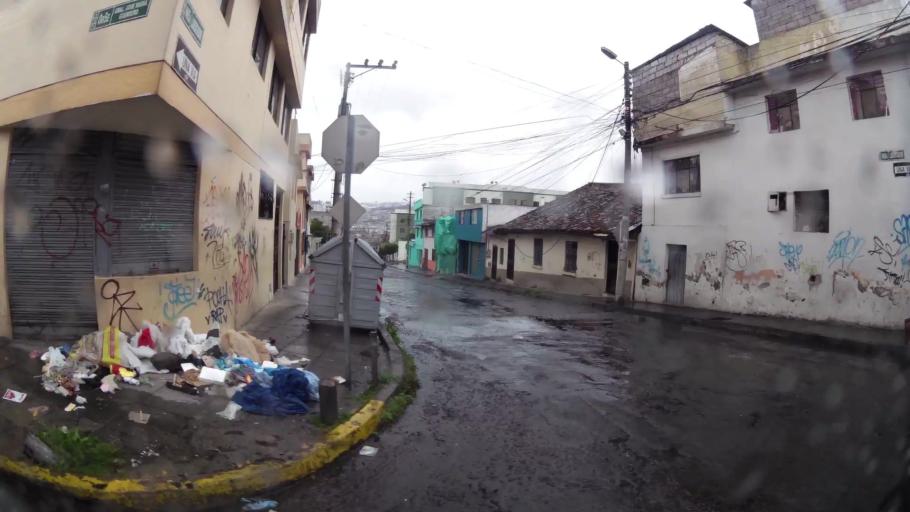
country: EC
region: Pichincha
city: Quito
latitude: -0.1162
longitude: -78.4973
